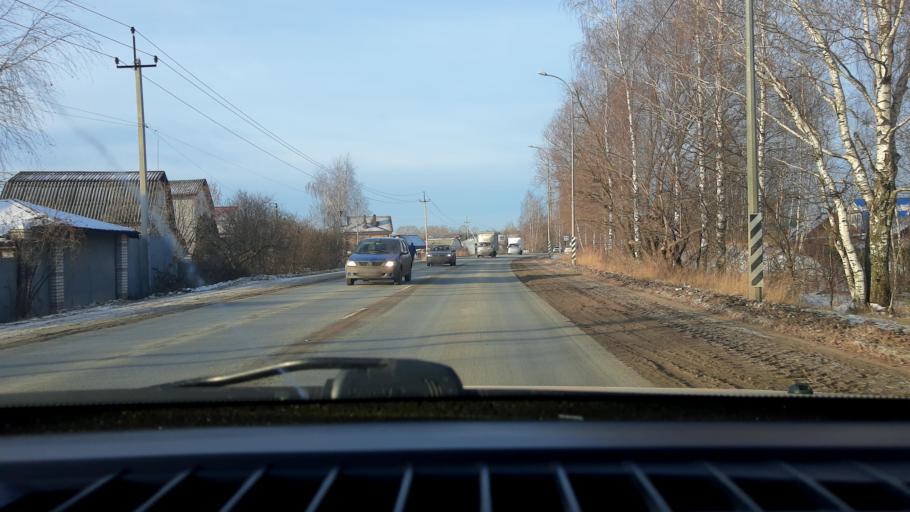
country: RU
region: Nizjnij Novgorod
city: Bor
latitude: 56.3791
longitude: 44.0456
